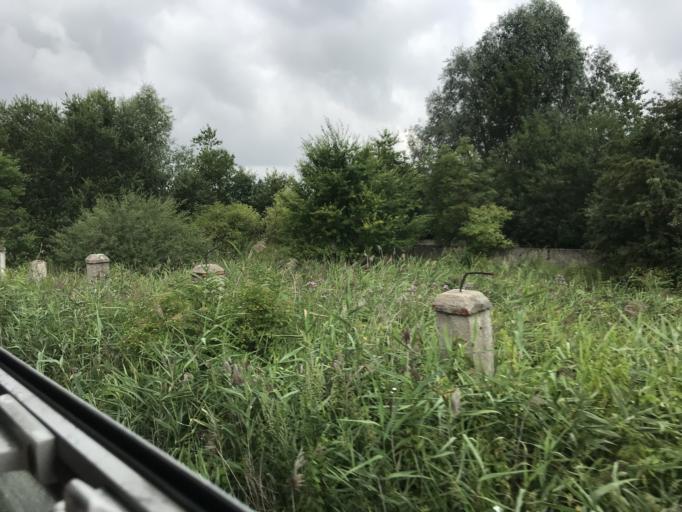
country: PL
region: Pomeranian Voivodeship
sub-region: Powiat malborski
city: Stare Pole
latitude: 54.0512
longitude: 19.1950
